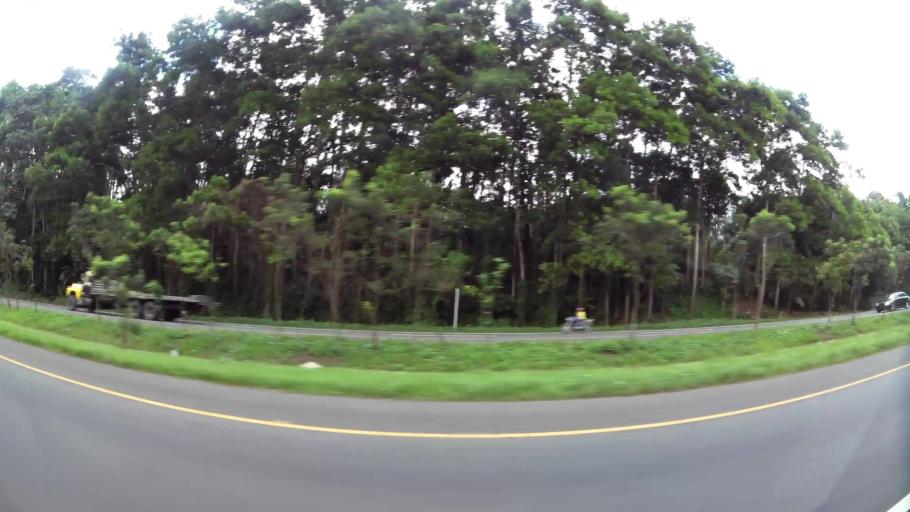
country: DO
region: Monsenor Nouel
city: Piedra Blanca
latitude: 18.8280
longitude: -70.2941
